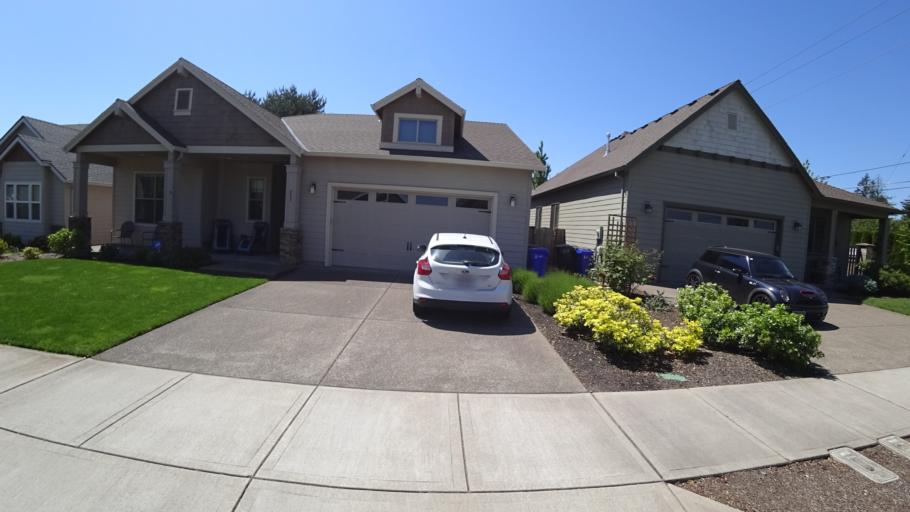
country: US
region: Oregon
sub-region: Washington County
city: Rockcreek
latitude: 45.5228
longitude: -122.9031
